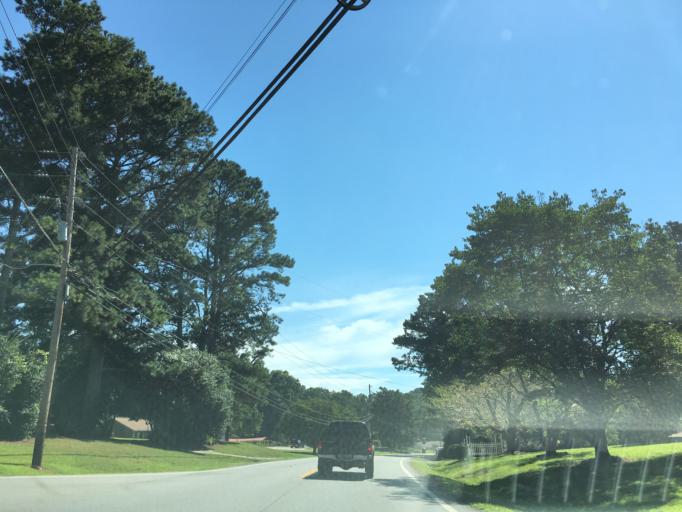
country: US
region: Georgia
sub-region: Fulton County
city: Milton
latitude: 34.1650
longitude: -84.2939
